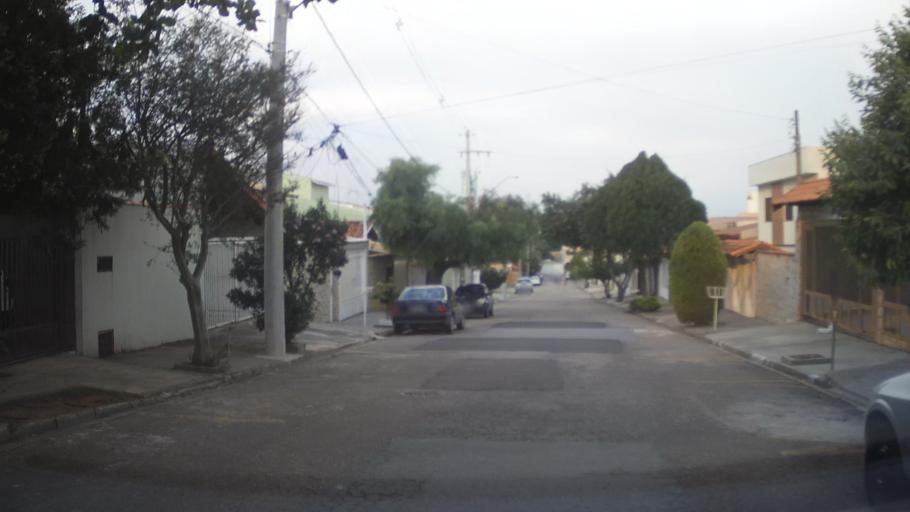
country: BR
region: Sao Paulo
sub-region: Jundiai
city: Jundiai
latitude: -23.1899
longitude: -46.9637
